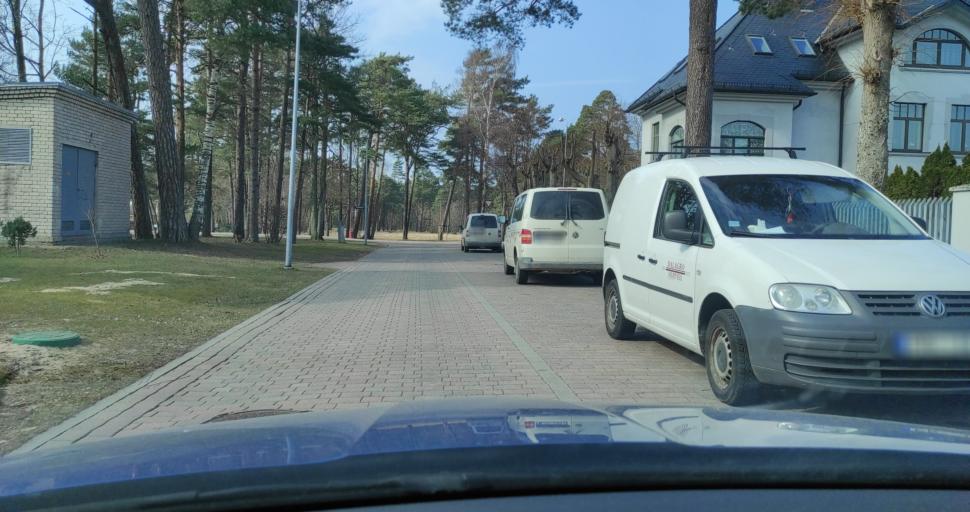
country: LV
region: Ventspils
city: Ventspils
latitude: 57.3856
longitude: 21.5409
